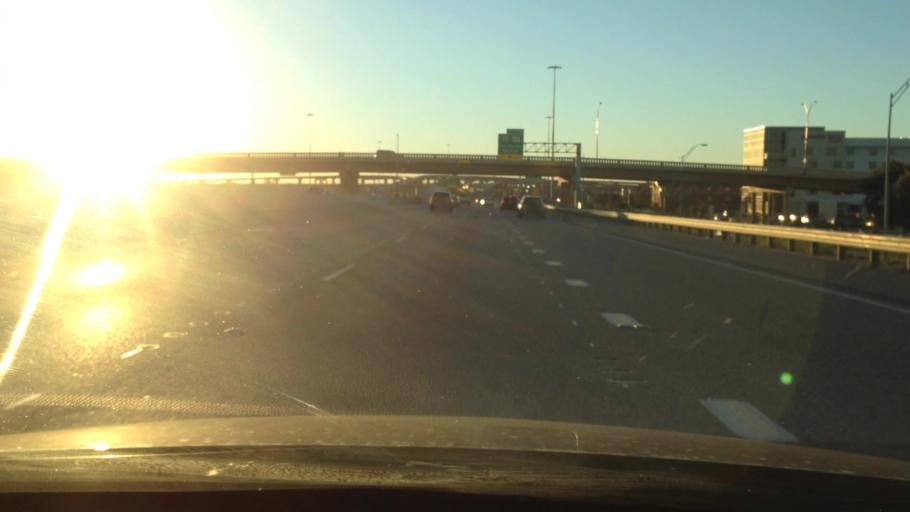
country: US
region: Texas
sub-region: Tarrant County
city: Blue Mound
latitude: 32.8396
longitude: -97.2984
